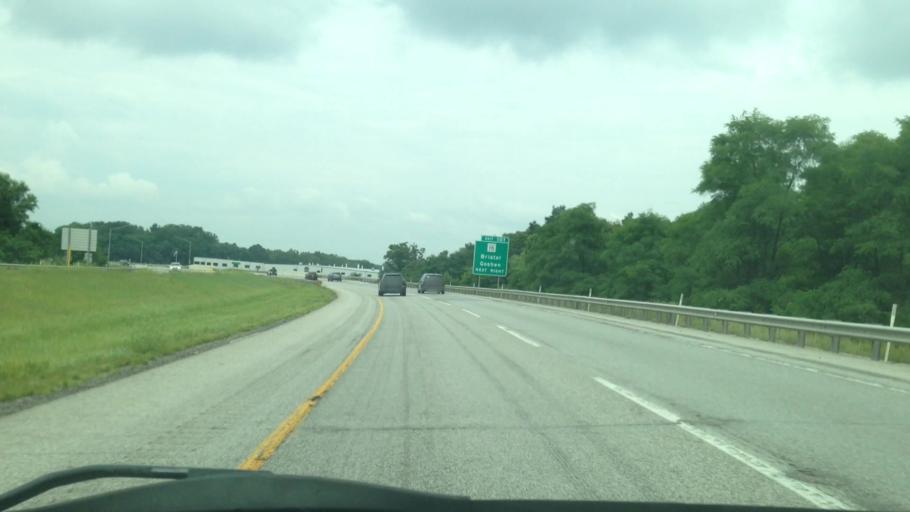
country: US
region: Indiana
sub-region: Elkhart County
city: Bristol
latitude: 41.7339
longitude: -85.7808
